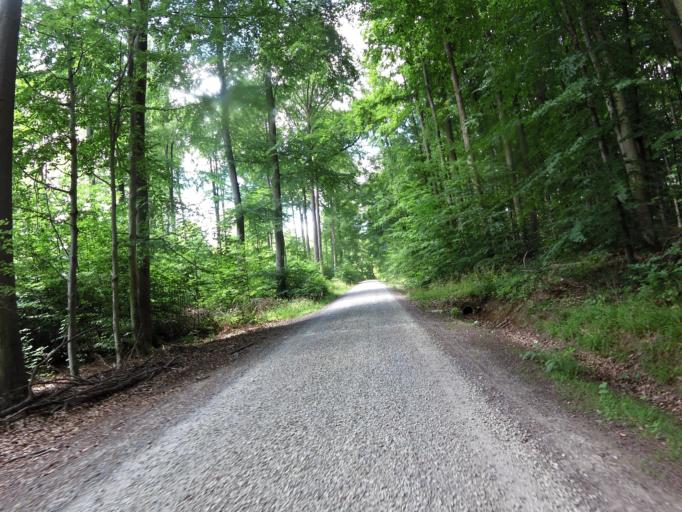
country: DE
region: Bavaria
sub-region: Regierungsbezirk Unterfranken
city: Wuerzburg
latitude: 49.7563
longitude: 9.8660
